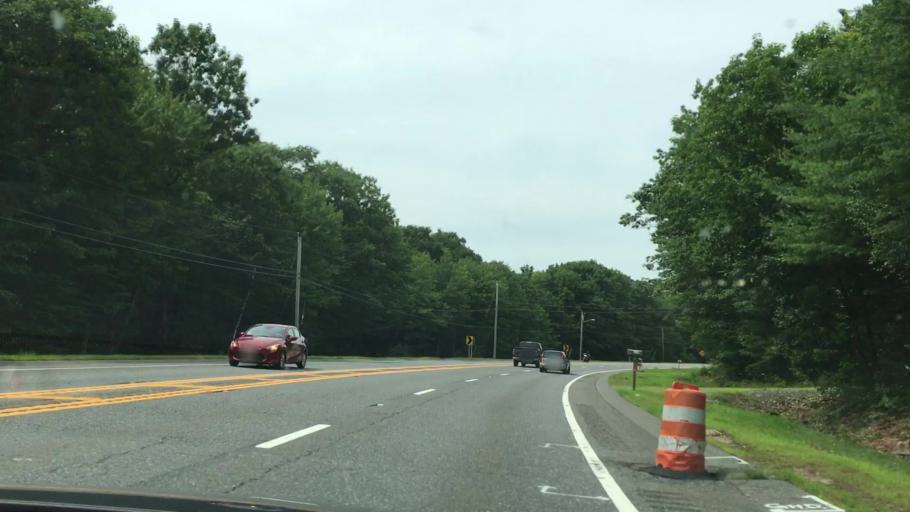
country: US
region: Massachusetts
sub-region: Worcester County
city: Gardner
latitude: 42.6176
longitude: -72.0075
